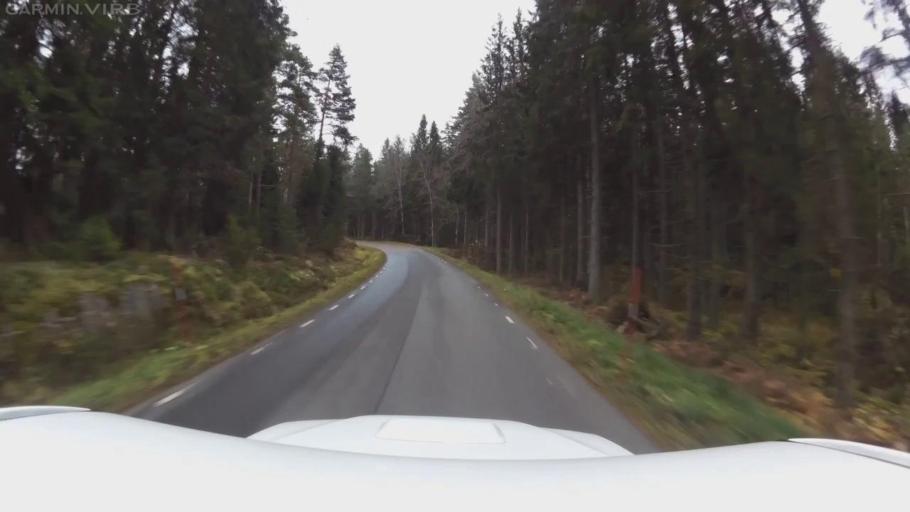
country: SE
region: OEstergoetland
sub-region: Mjolby Kommun
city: Mantorp
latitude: 58.1431
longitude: 15.3977
